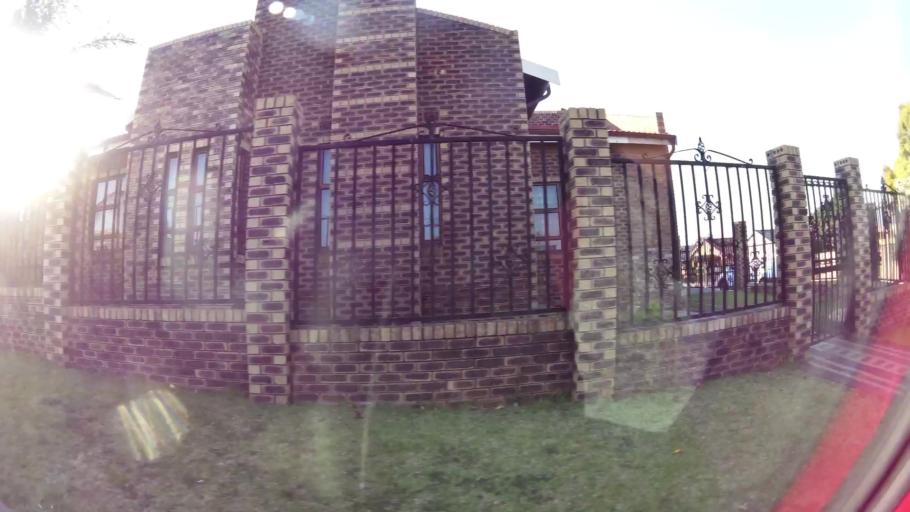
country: ZA
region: Gauteng
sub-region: City of Johannesburg Metropolitan Municipality
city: Soweto
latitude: -26.2519
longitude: 27.9540
